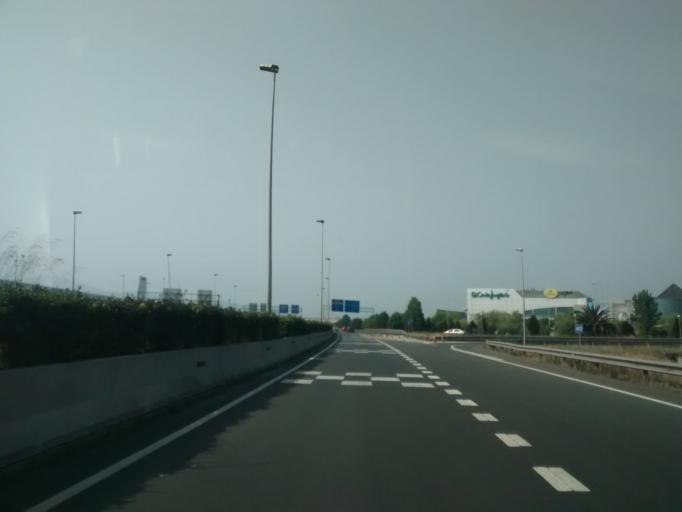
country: ES
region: Cantabria
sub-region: Provincia de Cantabria
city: Santander
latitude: 43.4402
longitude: -3.8369
